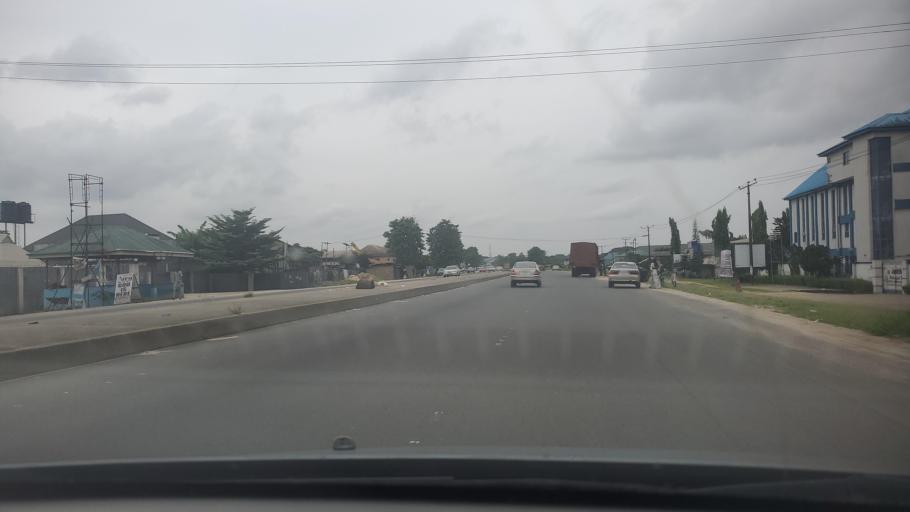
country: NG
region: Rivers
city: Emuoha
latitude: 4.8719
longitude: 6.9630
